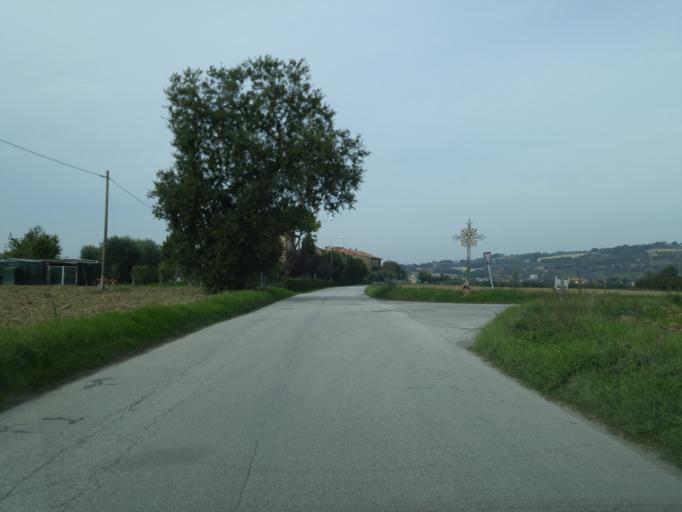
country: IT
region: The Marches
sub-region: Provincia di Pesaro e Urbino
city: Cuccurano
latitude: 43.7851
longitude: 12.9701
